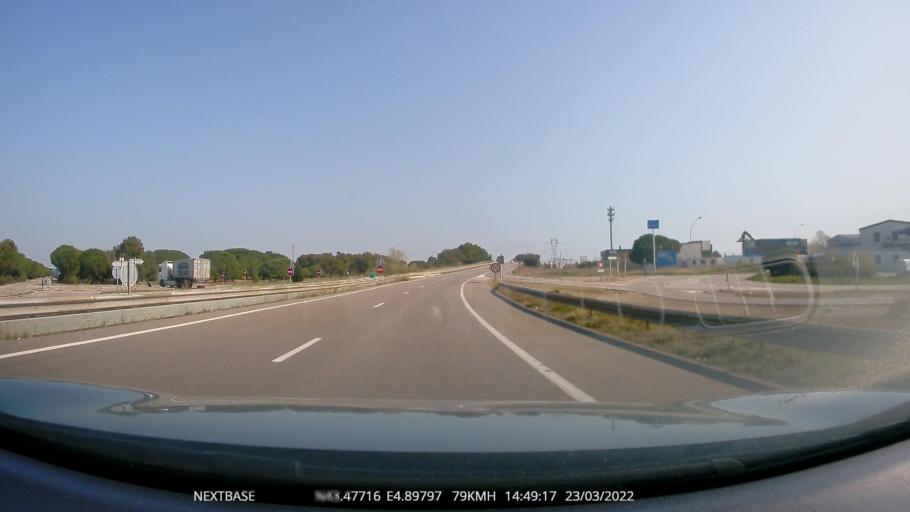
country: FR
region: Provence-Alpes-Cote d'Azur
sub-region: Departement des Bouches-du-Rhone
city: Fos-sur-Mer
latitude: 43.4771
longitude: 4.8978
